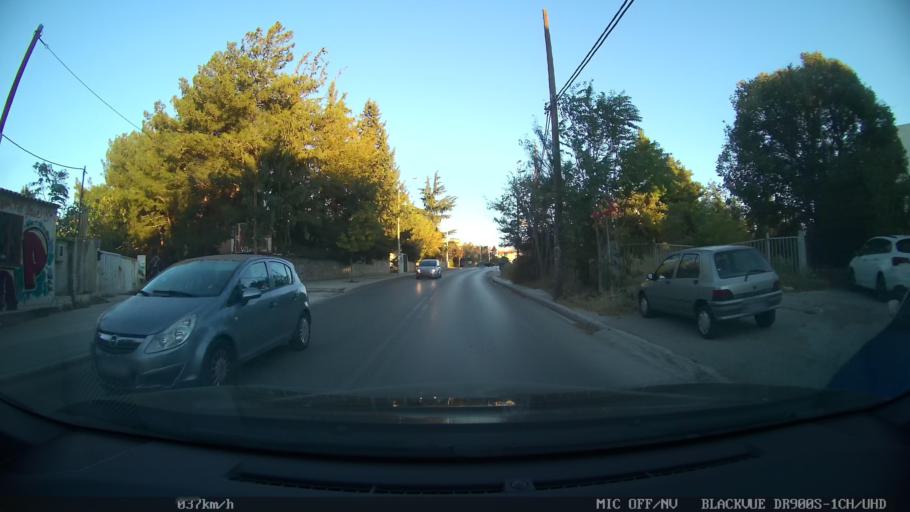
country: GR
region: Central Macedonia
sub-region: Nomos Thessalonikis
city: Pylaia
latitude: 40.6023
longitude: 22.9787
